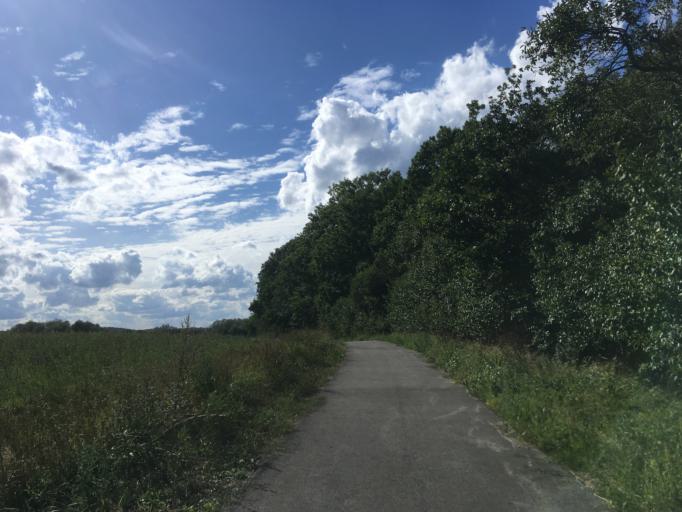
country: DE
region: Brandenburg
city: Liepe
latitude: 52.9083
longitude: 13.9976
